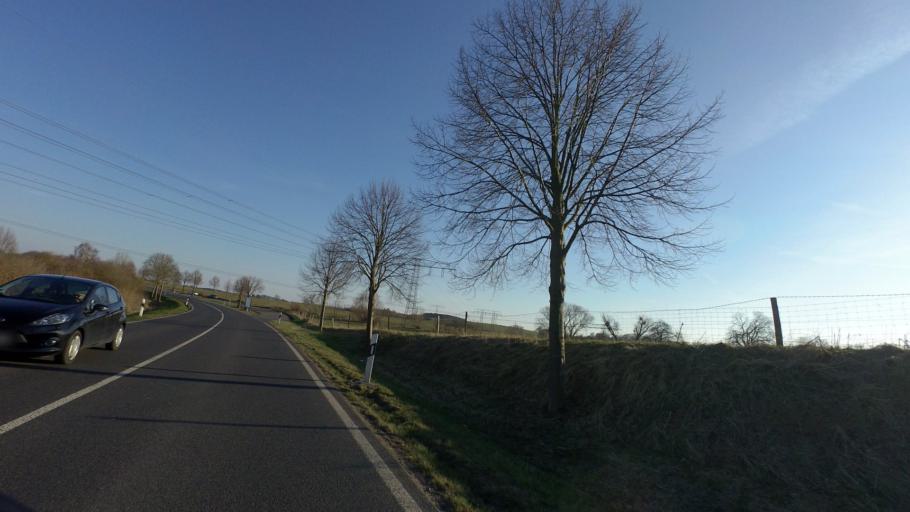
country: DE
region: Brandenburg
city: Britz
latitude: 52.9208
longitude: 13.7971
